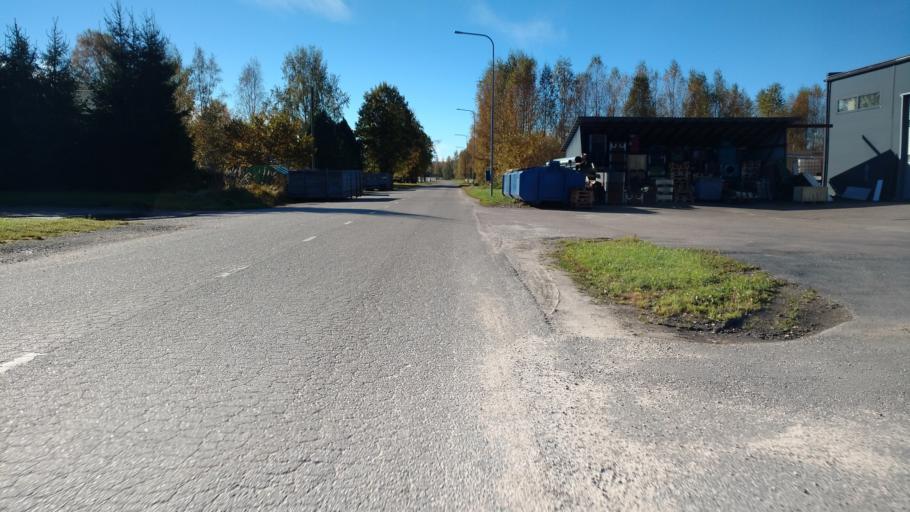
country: FI
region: Varsinais-Suomi
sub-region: Salo
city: Salo
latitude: 60.3999
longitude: 23.1670
